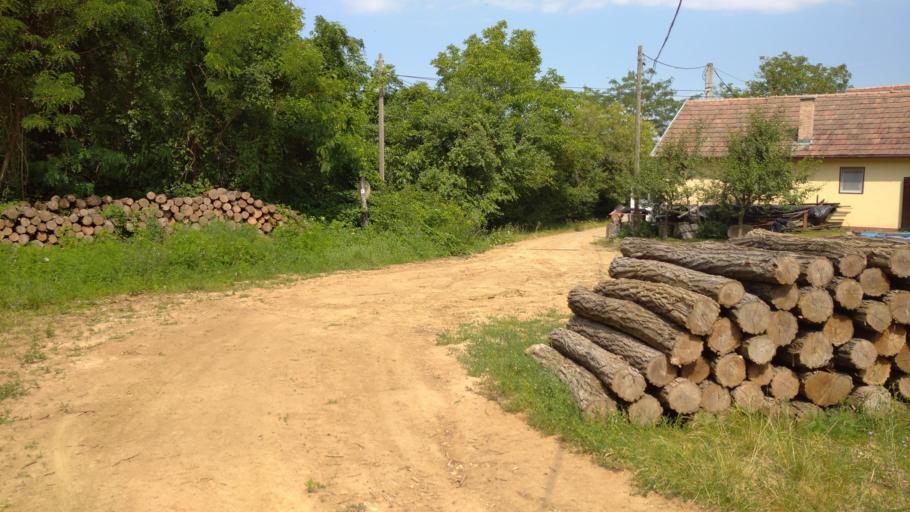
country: SK
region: Nitriansky
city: Sahy
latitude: 47.9891
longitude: 18.8621
